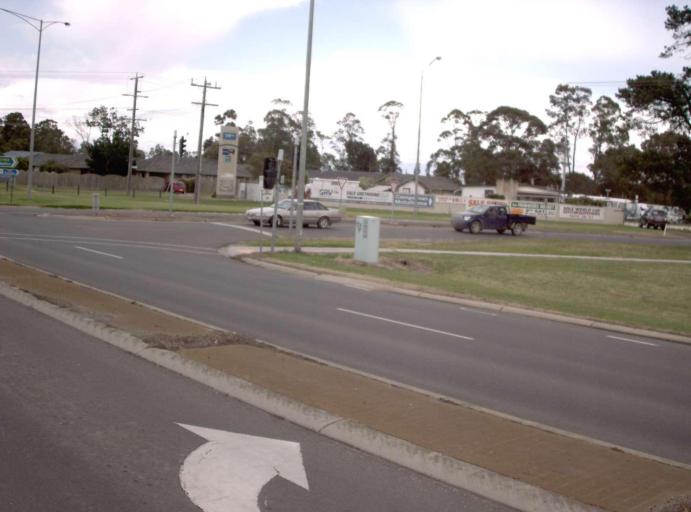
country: AU
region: Victoria
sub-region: Wellington
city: Sale
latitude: -38.0929
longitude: 147.0691
